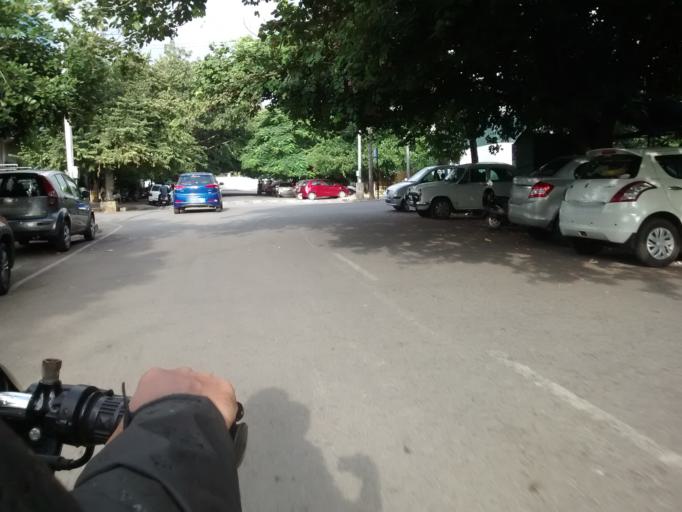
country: IN
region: Karnataka
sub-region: Bangalore Urban
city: Bangalore
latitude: 12.9422
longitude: 77.5726
